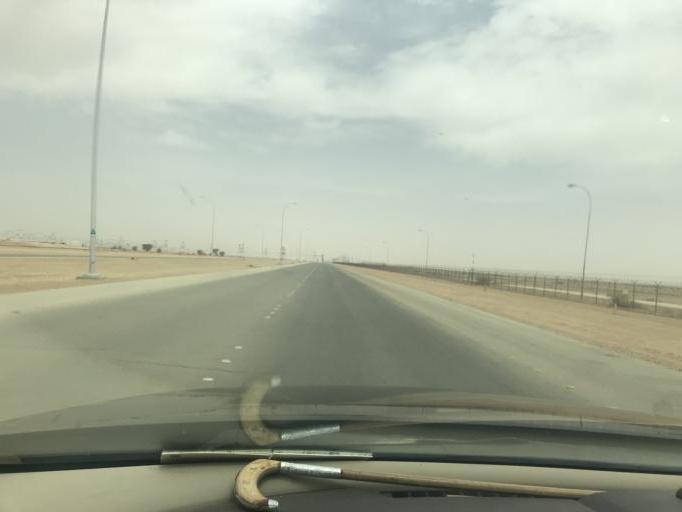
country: SA
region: Ar Riyad
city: Riyadh
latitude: 24.9643
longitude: 46.6674
